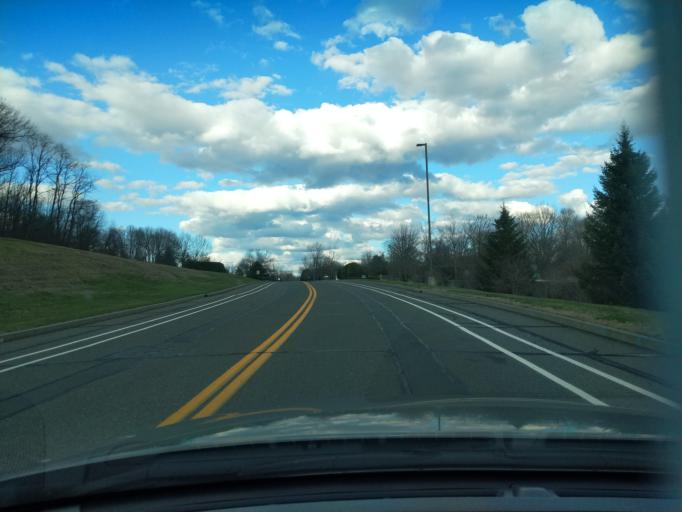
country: US
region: Connecticut
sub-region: Fairfield County
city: Bethel
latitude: 41.4248
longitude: -73.3985
